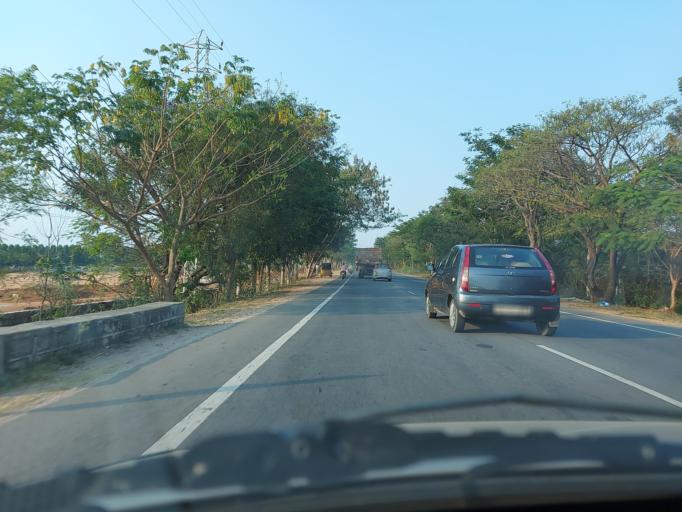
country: IN
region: Telangana
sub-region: Rangareddi
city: Balapur
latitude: 17.1454
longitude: 78.4791
